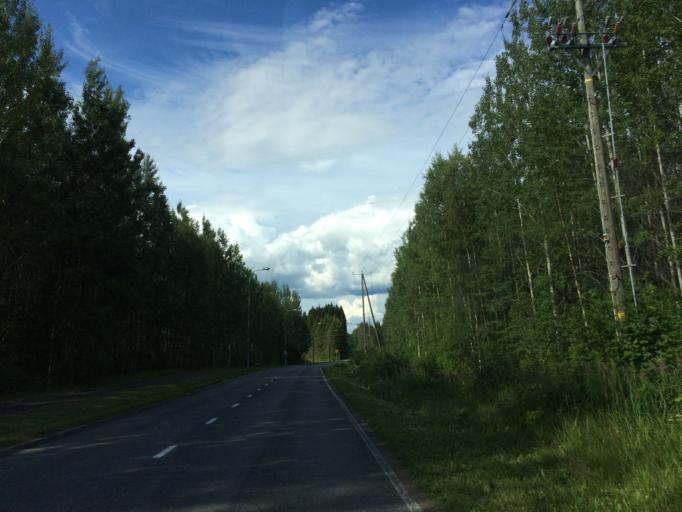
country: FI
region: Haeme
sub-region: Haemeenlinna
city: Janakkala
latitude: 60.9103
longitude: 24.6113
